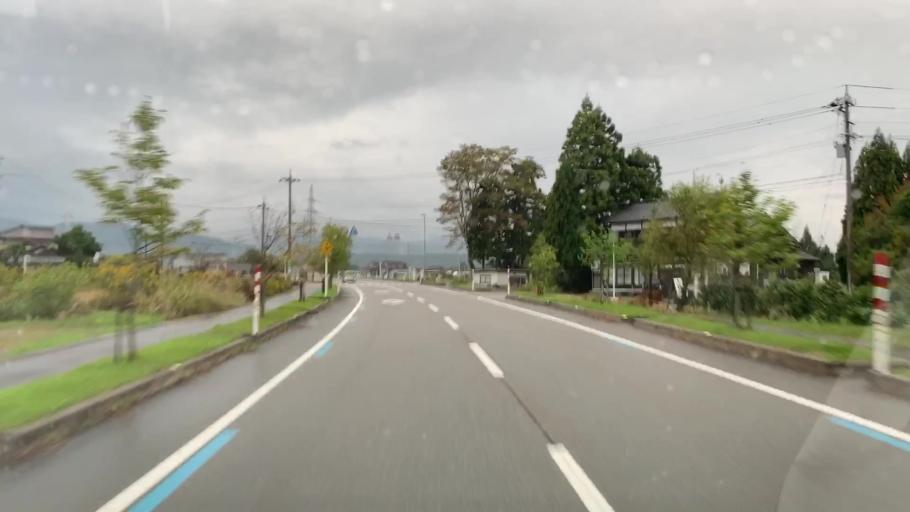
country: JP
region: Toyama
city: Kamiichi
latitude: 36.6134
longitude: 137.3249
